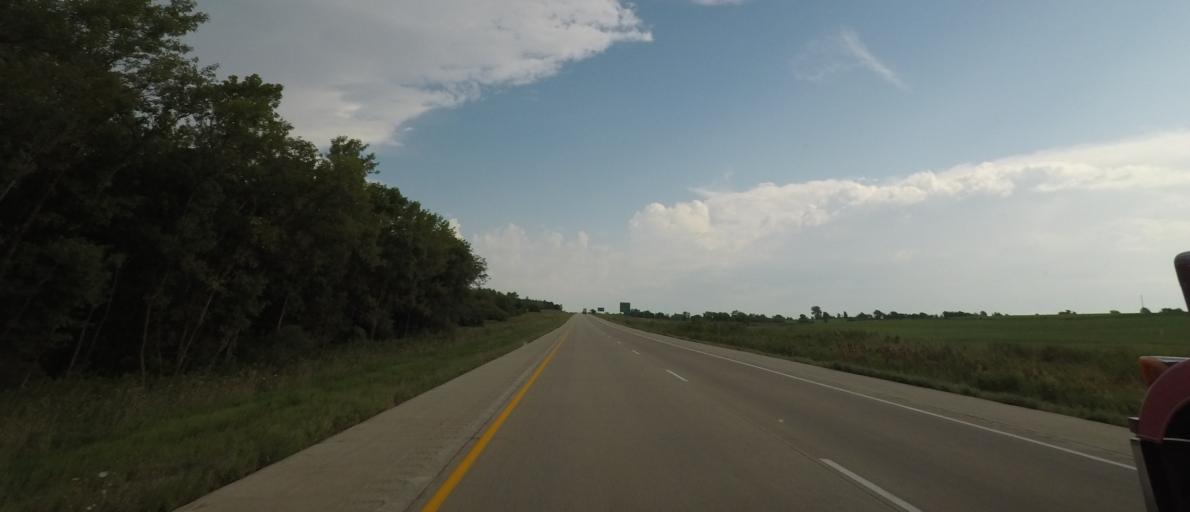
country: US
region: Iowa
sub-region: Decatur County
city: Lamoni
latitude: 40.6095
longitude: -93.9008
